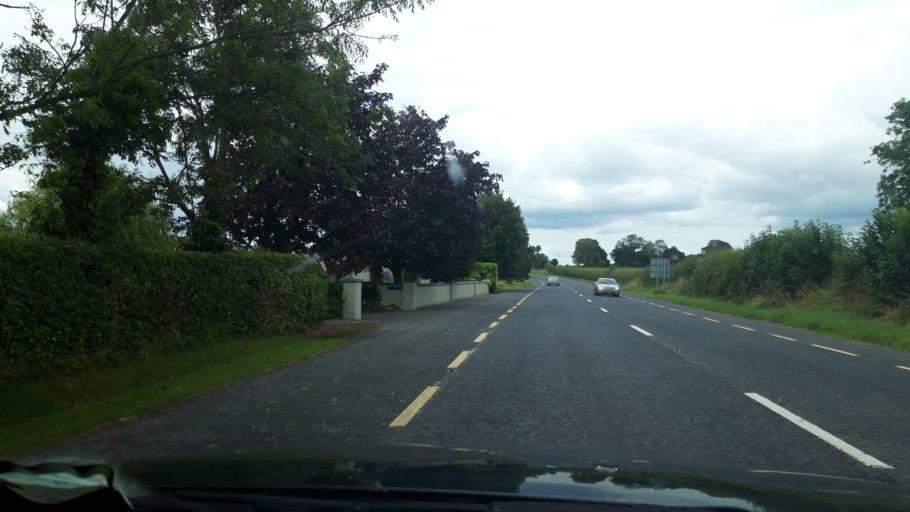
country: IE
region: Leinster
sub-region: County Carlow
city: Bagenalstown
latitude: 52.6439
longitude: -7.0555
